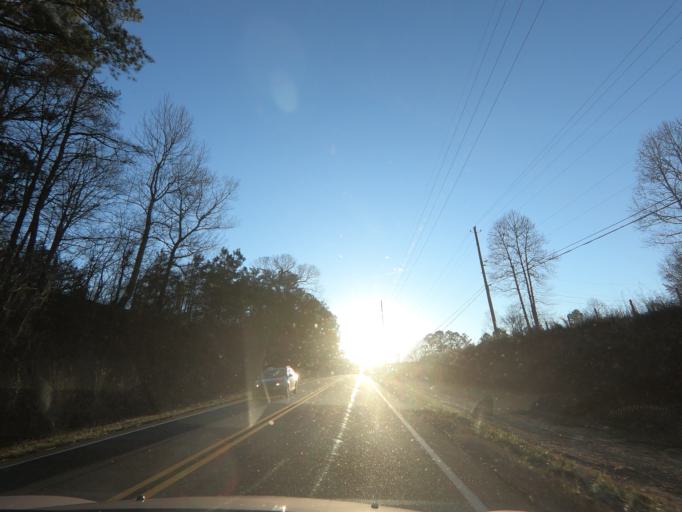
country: US
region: Georgia
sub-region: Dawson County
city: Dawsonville
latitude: 34.3511
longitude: -84.1029
